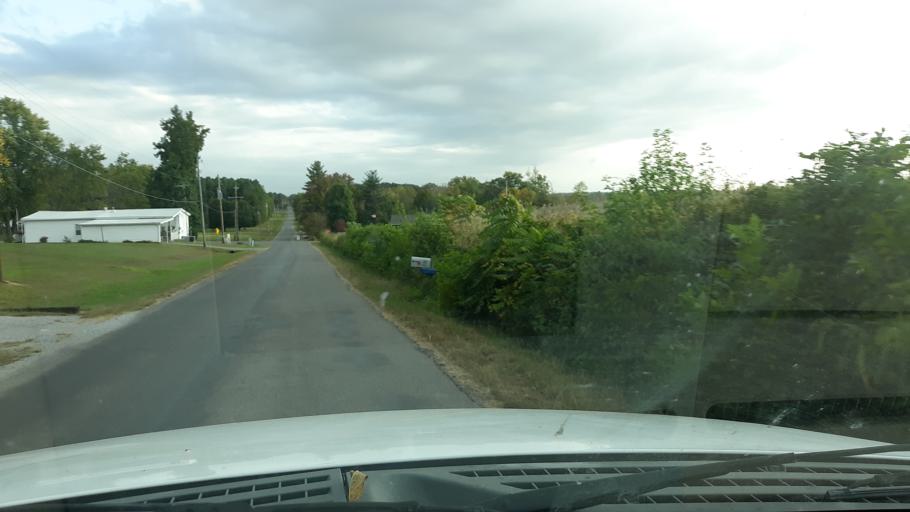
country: US
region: Illinois
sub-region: Saline County
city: Eldorado
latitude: 37.8252
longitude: -88.5025
